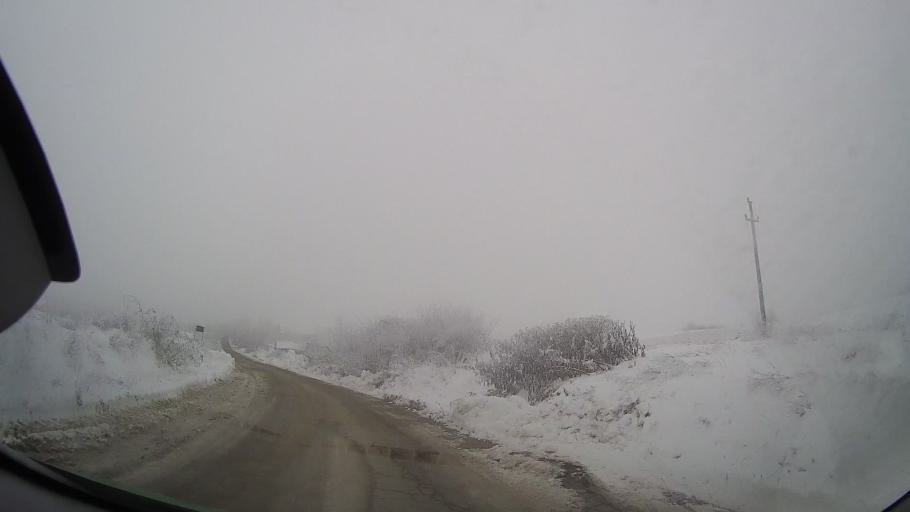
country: RO
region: Iasi
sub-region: Comuna Dagata
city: Dagata
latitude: 46.9225
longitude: 27.1675
